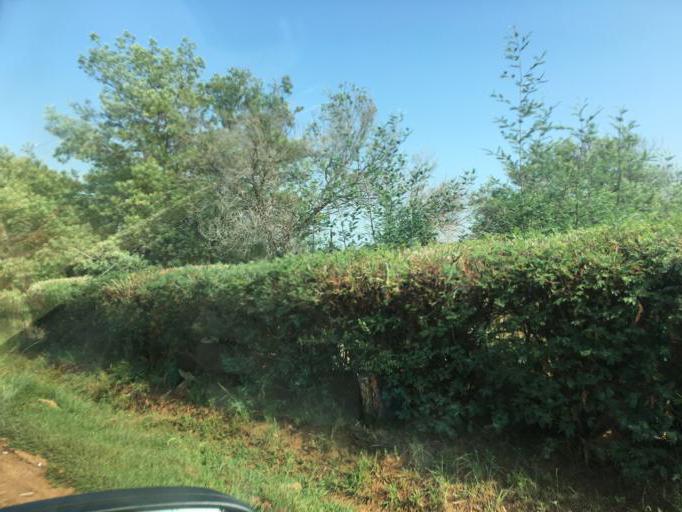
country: LS
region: Maseru
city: Maseru
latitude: -29.4482
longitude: 27.5630
